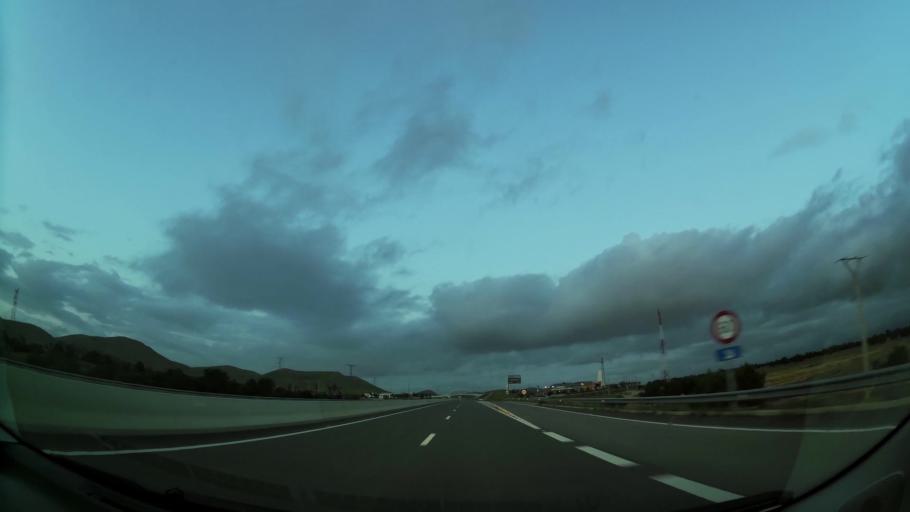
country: MA
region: Oriental
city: El Aioun
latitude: 34.6165
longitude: -2.4442
